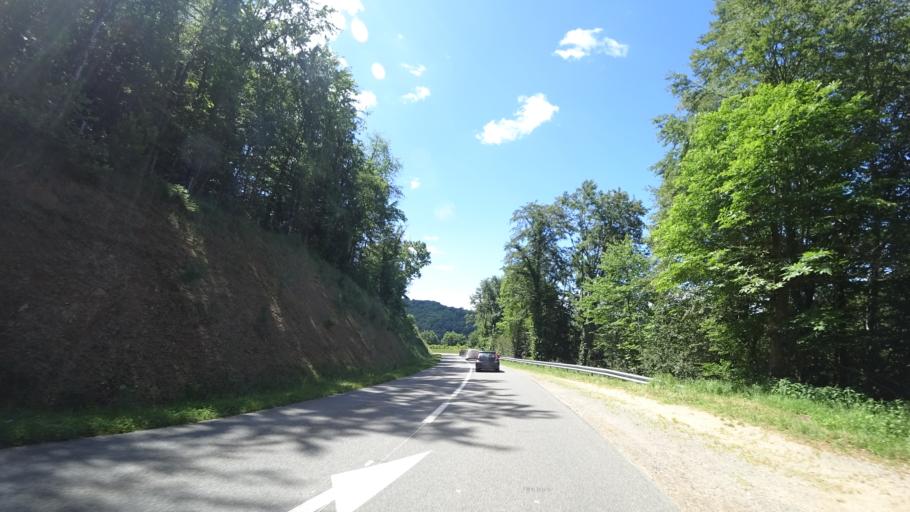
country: FR
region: Midi-Pyrenees
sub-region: Departement de l'Aveyron
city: Colombies
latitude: 44.3839
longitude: 2.3042
